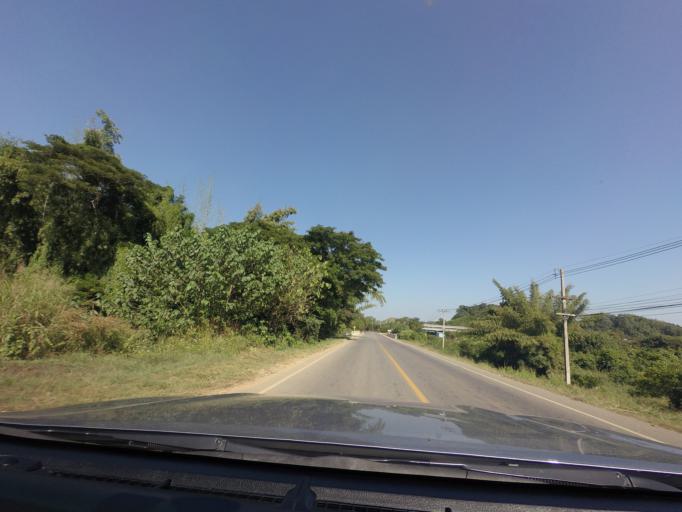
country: TH
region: Sukhothai
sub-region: Amphoe Si Satchanalai
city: Si Satchanalai
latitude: 17.6764
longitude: 99.7005
